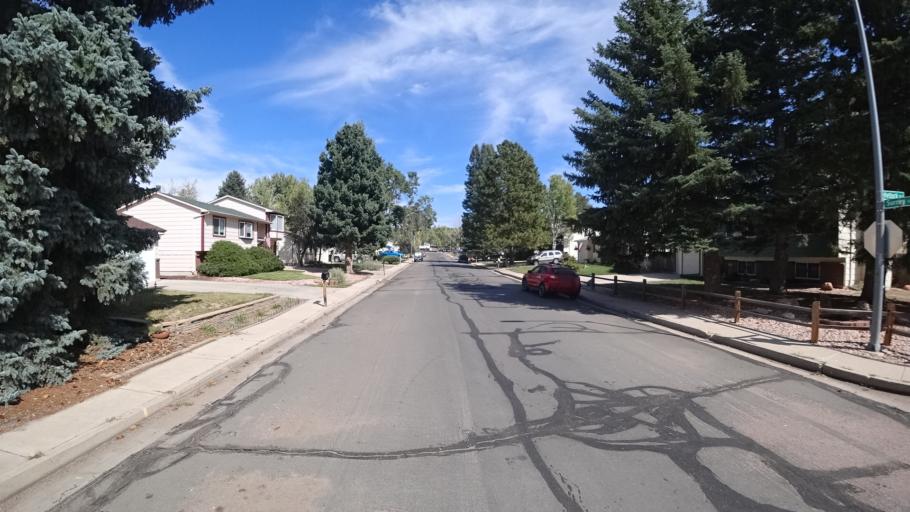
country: US
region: Colorado
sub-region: El Paso County
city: Cimarron Hills
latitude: 38.8998
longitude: -104.7557
